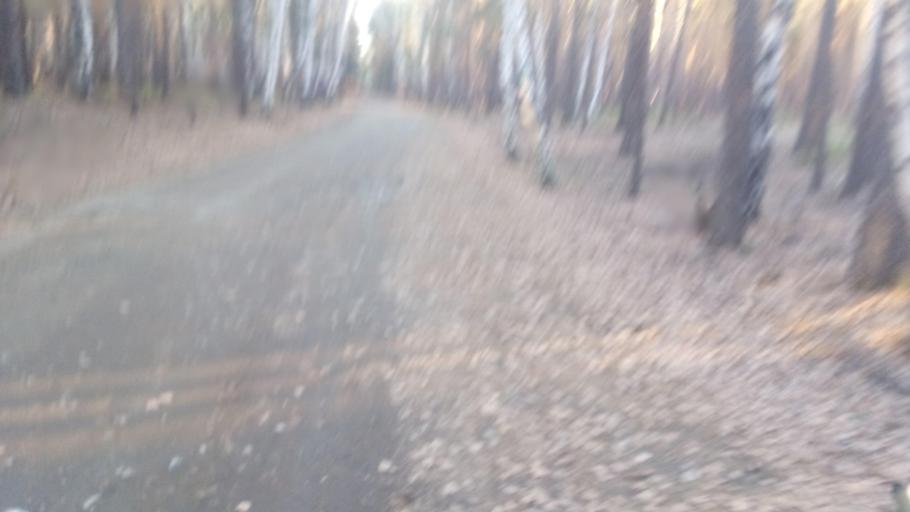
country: RU
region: Chelyabinsk
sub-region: Gorod Chelyabinsk
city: Chelyabinsk
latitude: 55.1247
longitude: 61.3459
